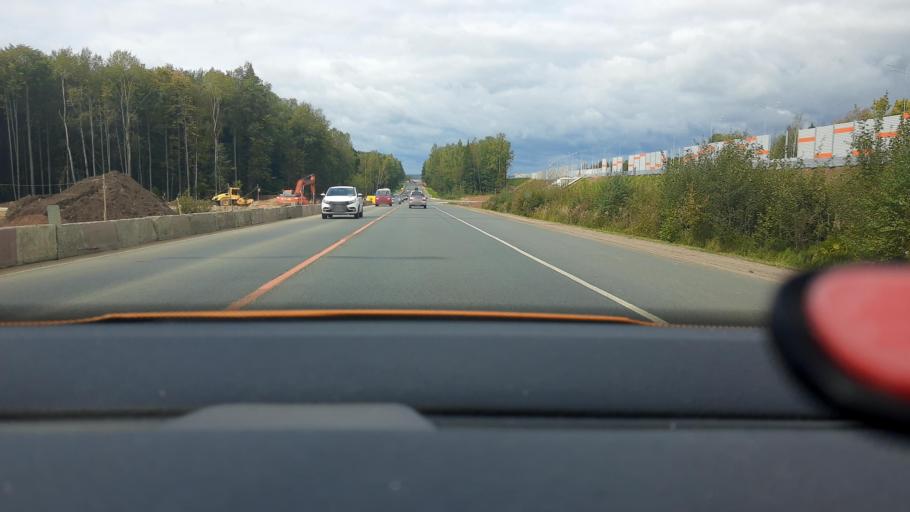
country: RU
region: Moskovskaya
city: Zelenogradskiy
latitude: 56.0974
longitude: 37.9765
